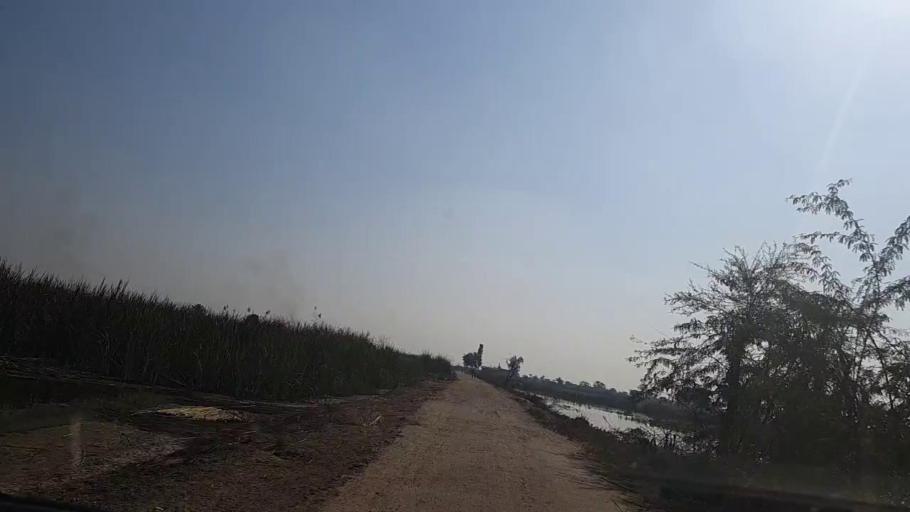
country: PK
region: Sindh
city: Sakrand
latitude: 26.0893
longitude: 68.3704
